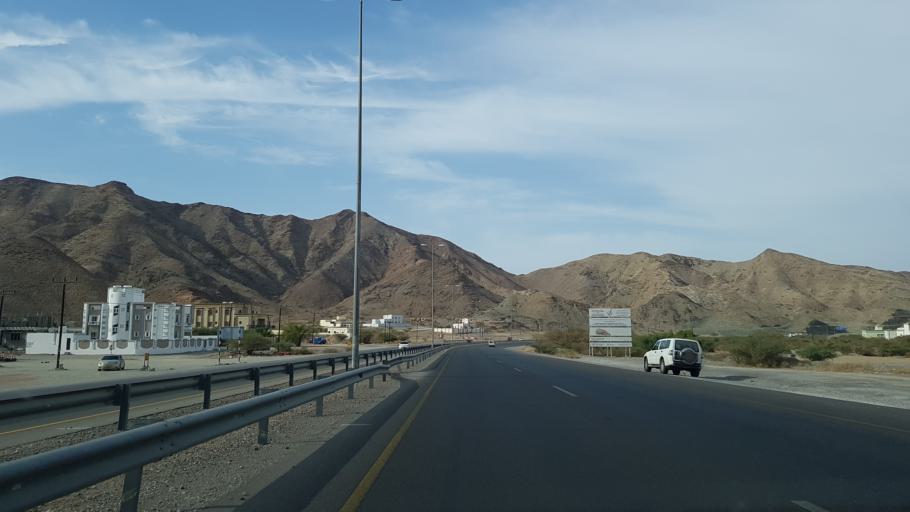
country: OM
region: Muhafazat ad Dakhiliyah
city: Bidbid
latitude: 23.4075
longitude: 58.0804
